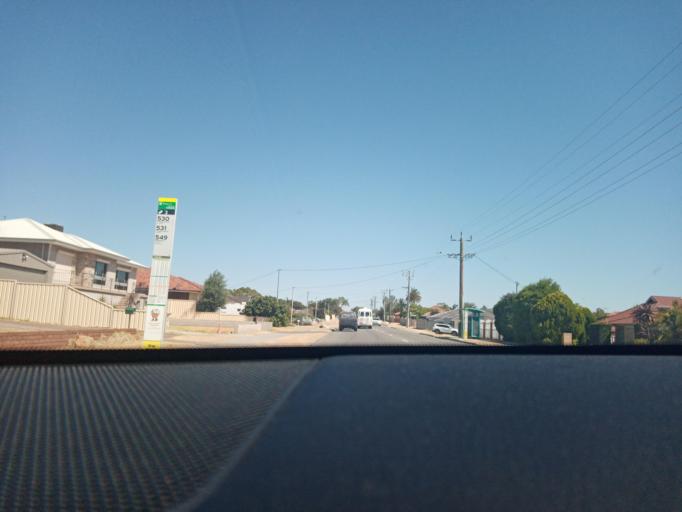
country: AU
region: Western Australia
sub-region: City of Cockburn
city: Coogee
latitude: -32.1252
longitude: 115.7851
